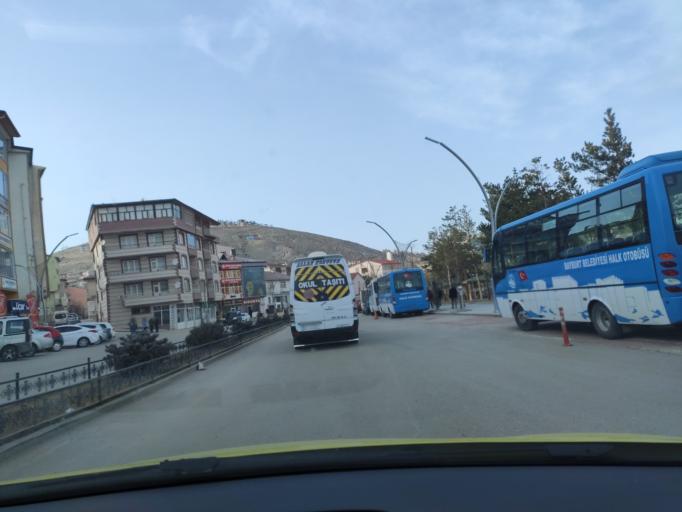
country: TR
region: Bayburt
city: Bayburt
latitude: 40.2544
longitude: 40.2260
